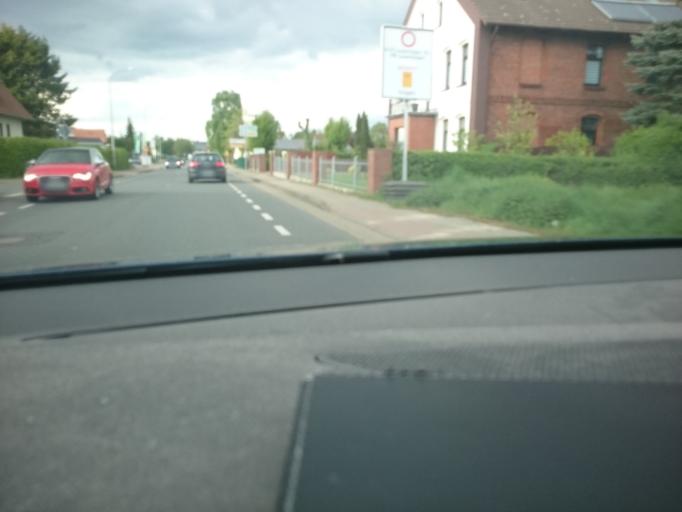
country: DE
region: Lower Saxony
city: Stadthagen
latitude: 52.3261
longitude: 9.2158
